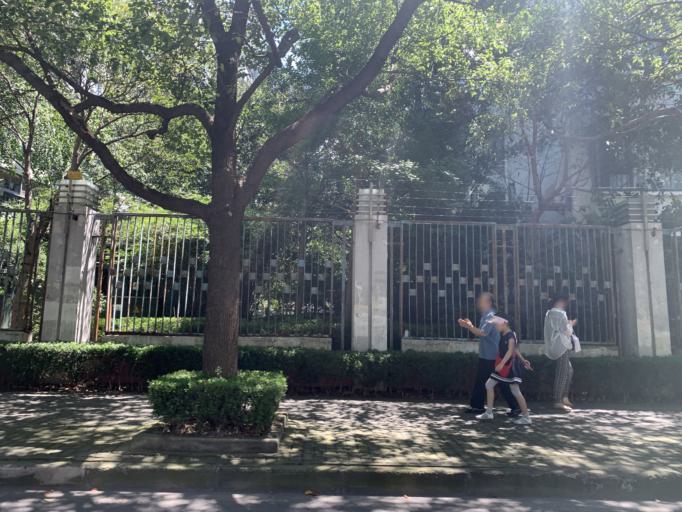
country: CN
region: Shanghai Shi
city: Huamu
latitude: 31.1803
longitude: 121.5334
